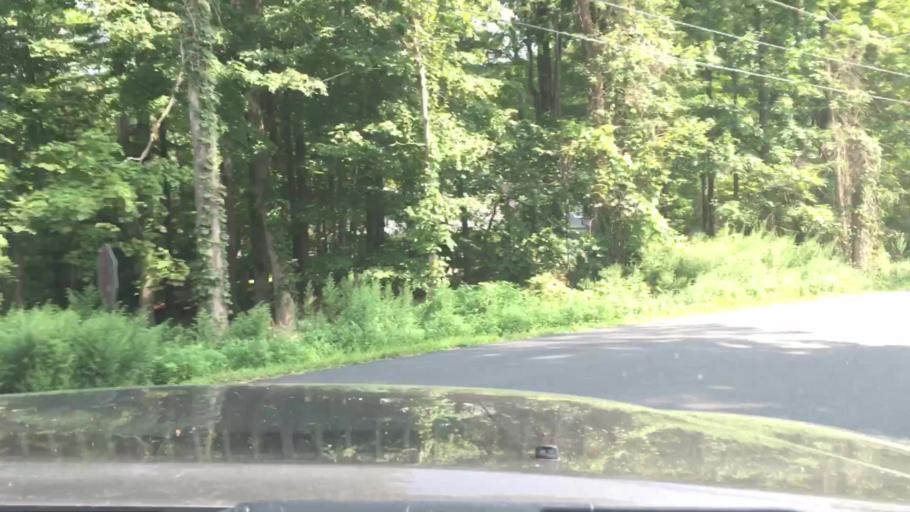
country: US
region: Connecticut
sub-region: Fairfield County
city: Georgetown
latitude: 41.2659
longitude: -73.4553
